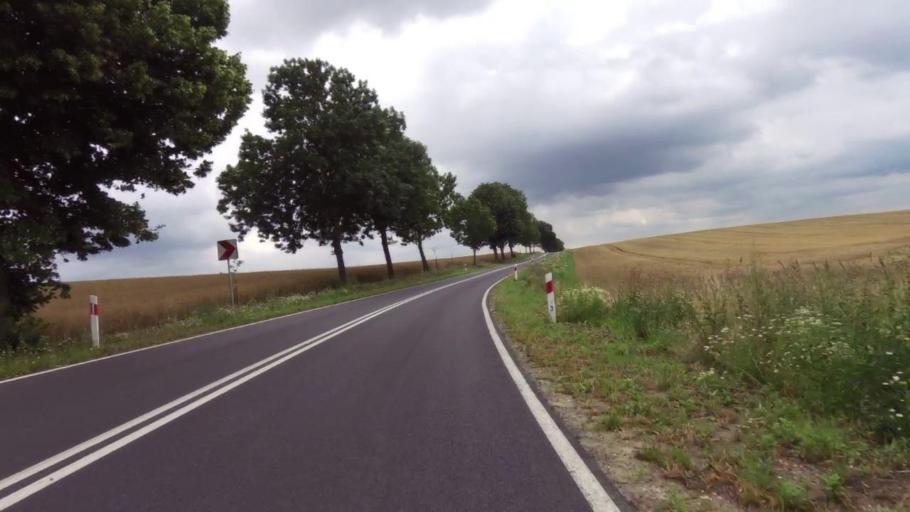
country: PL
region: West Pomeranian Voivodeship
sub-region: Powiat gryfinski
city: Cedynia
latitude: 52.8679
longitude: 14.2531
